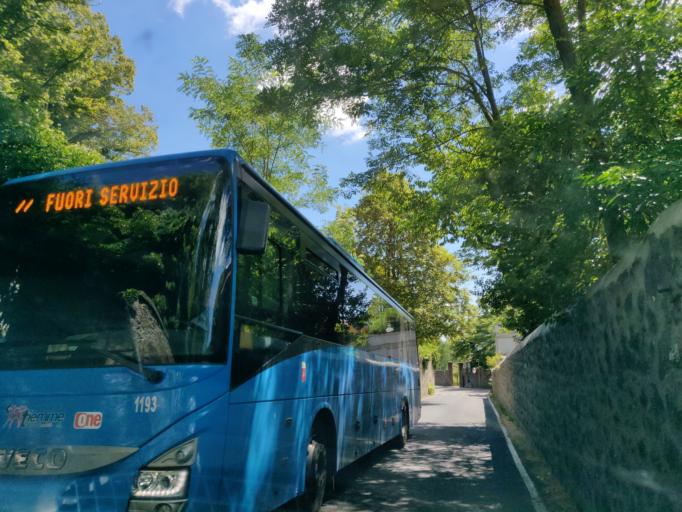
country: IT
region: Tuscany
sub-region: Provincia di Siena
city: Abbadia San Salvatore
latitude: 42.8826
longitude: 11.6668
